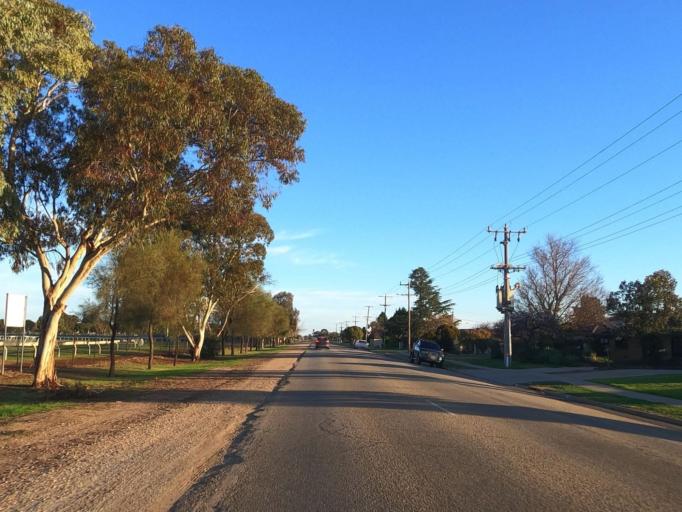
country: AU
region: Victoria
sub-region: Swan Hill
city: Swan Hill
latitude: -35.3510
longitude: 143.5541
